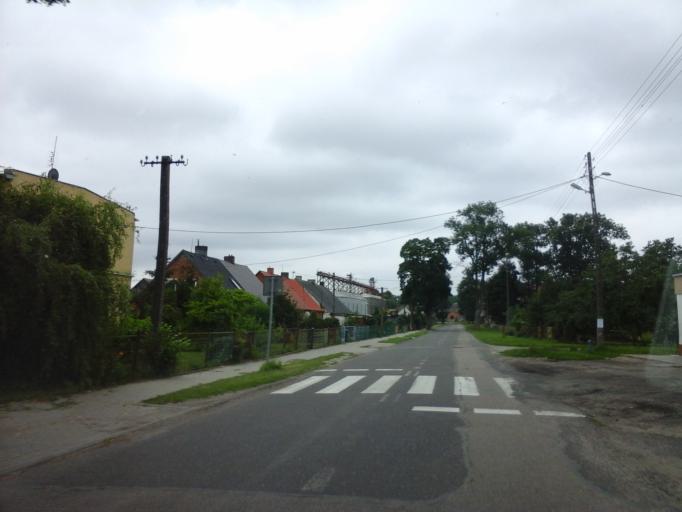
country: PL
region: West Pomeranian Voivodeship
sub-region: Powiat stargardzki
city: Dolice
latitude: 53.1176
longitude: 15.2521
